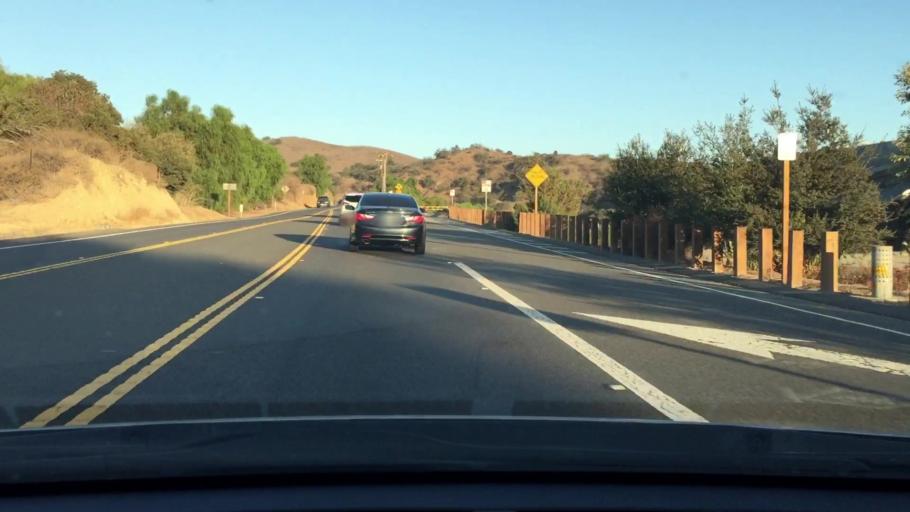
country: US
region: California
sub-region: Orange County
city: Yorba Linda
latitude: 33.9207
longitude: -117.8274
